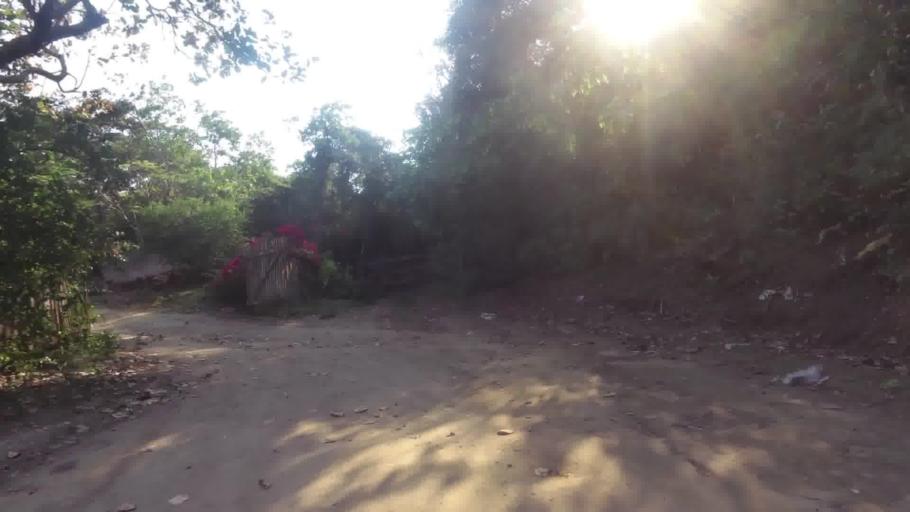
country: BR
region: Espirito Santo
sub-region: Piuma
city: Piuma
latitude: -20.8561
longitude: -40.7545
